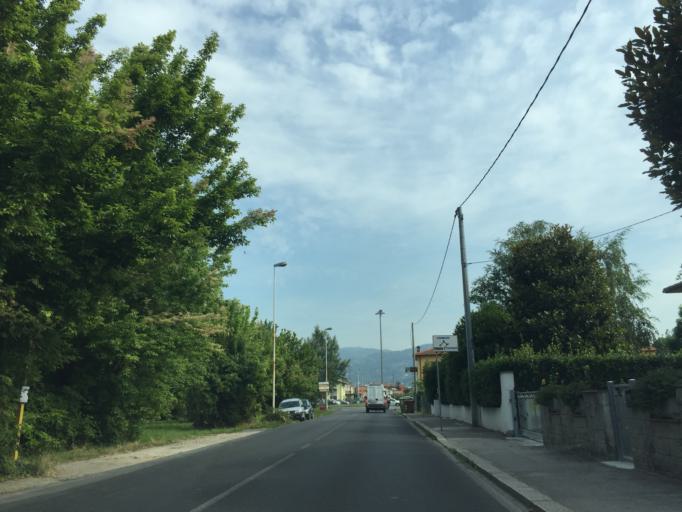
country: IT
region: Tuscany
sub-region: Provincia di Pistoia
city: Montecatini-Terme
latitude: 43.8674
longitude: 10.7671
